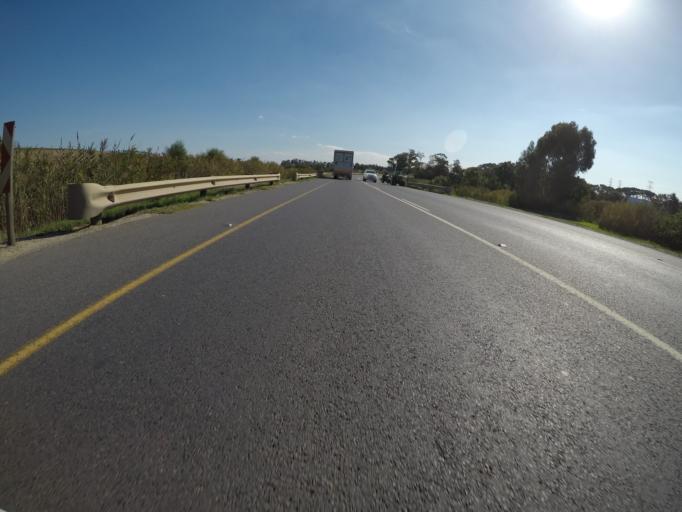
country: ZA
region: Western Cape
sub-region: City of Cape Town
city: Kraaifontein
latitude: -33.9026
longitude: 18.7219
